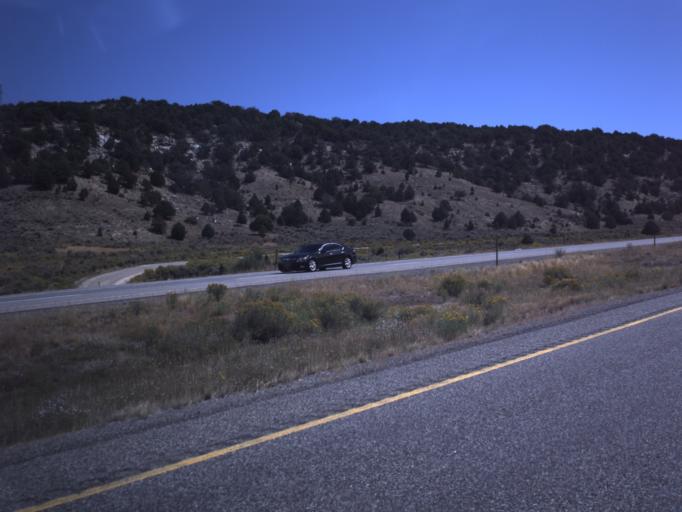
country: US
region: Utah
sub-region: Sevier County
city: Salina
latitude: 38.8099
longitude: -111.5342
